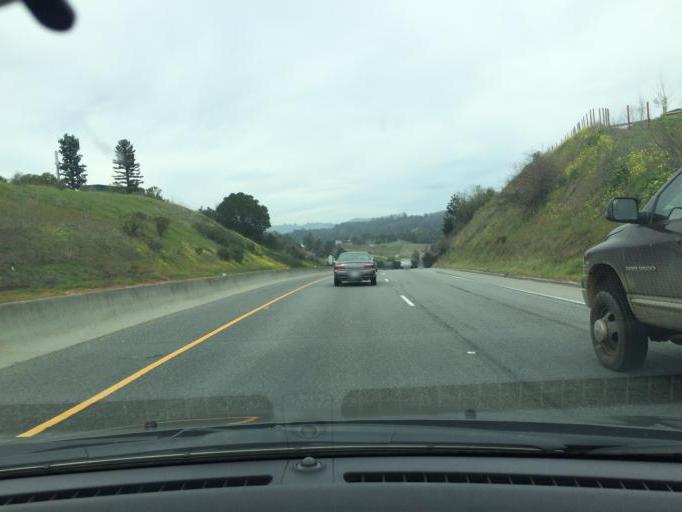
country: US
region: California
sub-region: San Benito County
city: Aromas
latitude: 36.8497
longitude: -121.6361
